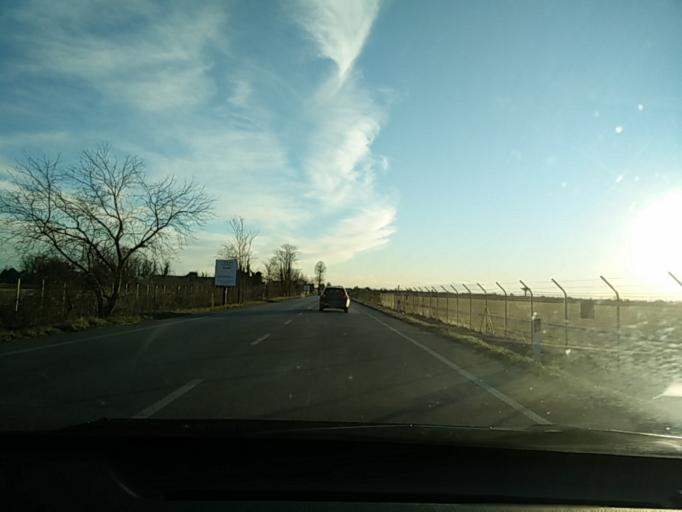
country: IT
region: Friuli Venezia Giulia
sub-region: Provincia di Udine
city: Pasian di Prato
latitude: 46.0323
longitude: 13.1785
